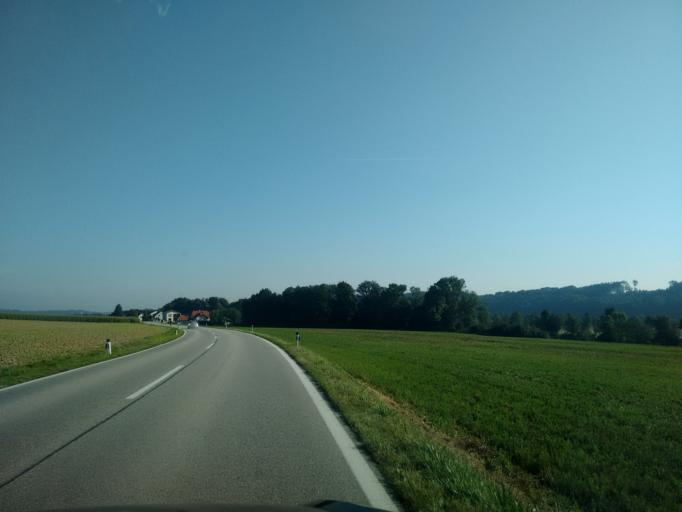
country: AT
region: Upper Austria
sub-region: Politischer Bezirk Steyr-Land
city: Bad Hall
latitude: 48.0817
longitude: 14.1914
